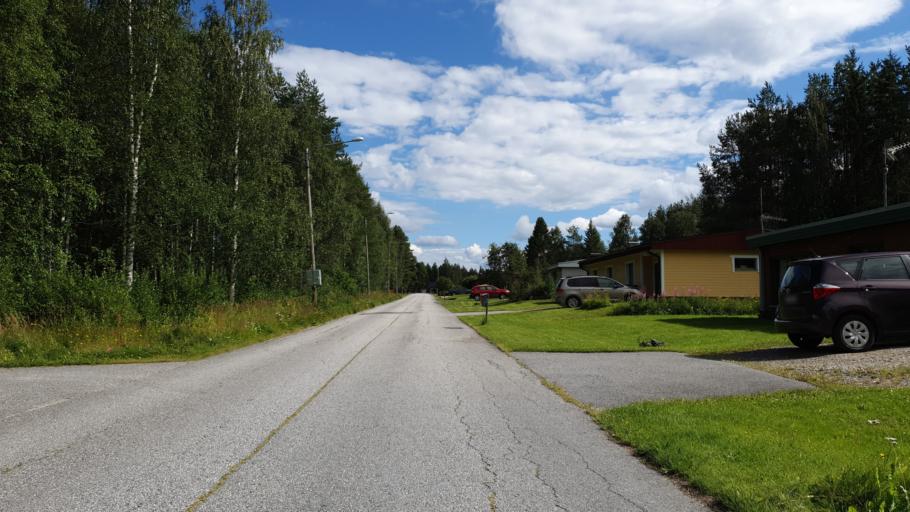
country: FI
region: Kainuu
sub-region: Kehys-Kainuu
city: Kuhmo
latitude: 64.1156
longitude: 29.4864
